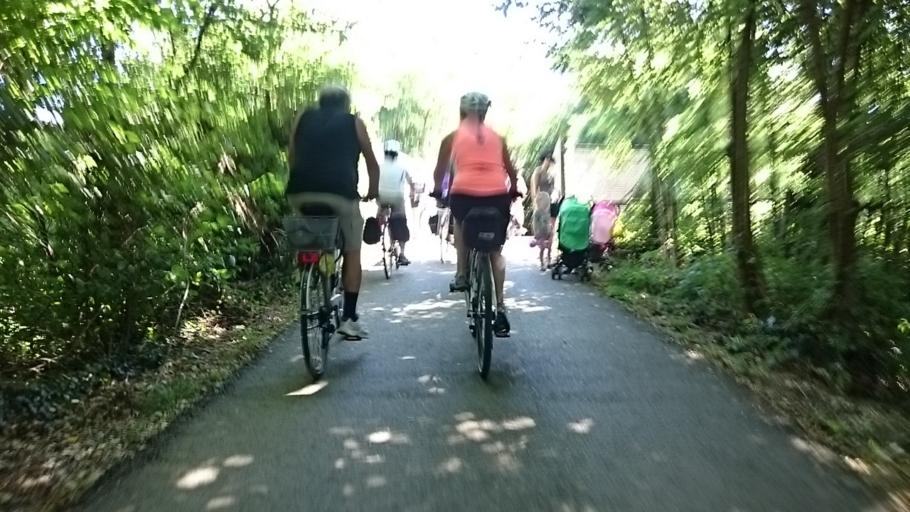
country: IT
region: Veneto
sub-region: Provincia di Padova
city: Piombino Dese
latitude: 45.6031
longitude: 12.0087
